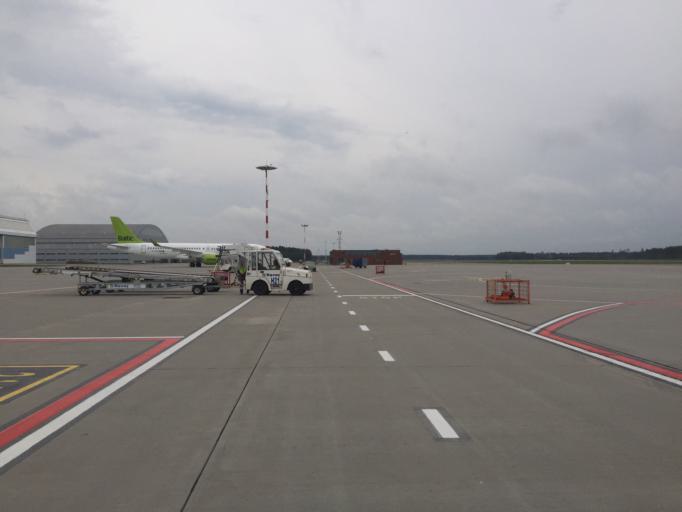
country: LV
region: Babite
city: Pinki
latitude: 56.9187
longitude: 23.9760
